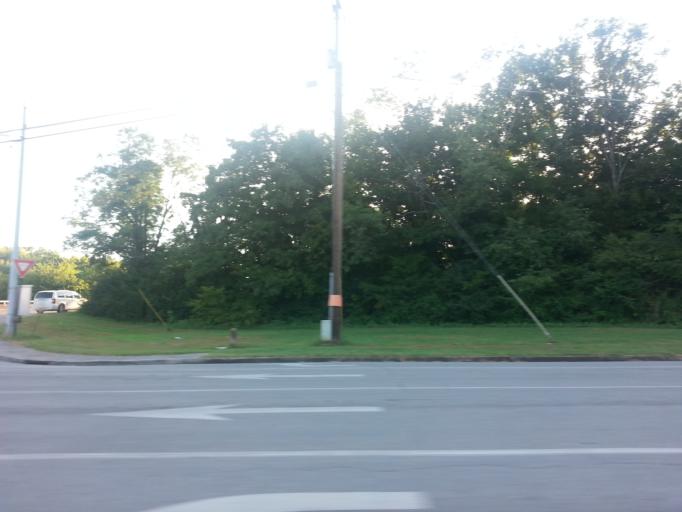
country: US
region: Tennessee
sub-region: McMinn County
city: Athens
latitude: 35.4494
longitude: -84.5972
